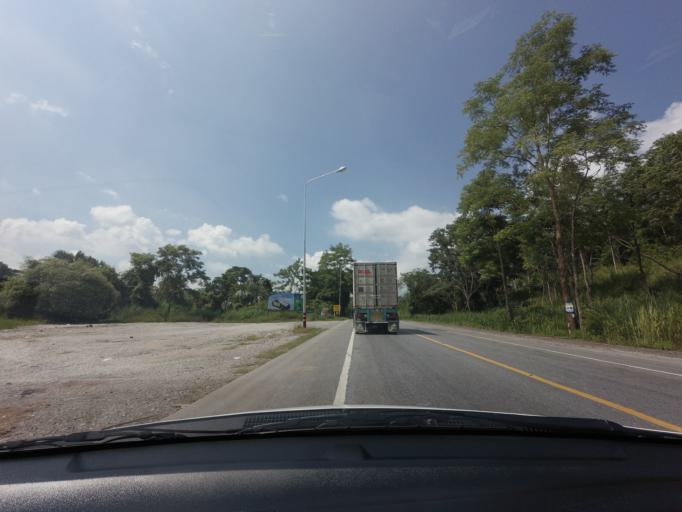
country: TH
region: Nakhon Ratchasima
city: Wang Nam Khiao
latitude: 14.2971
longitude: 101.8804
